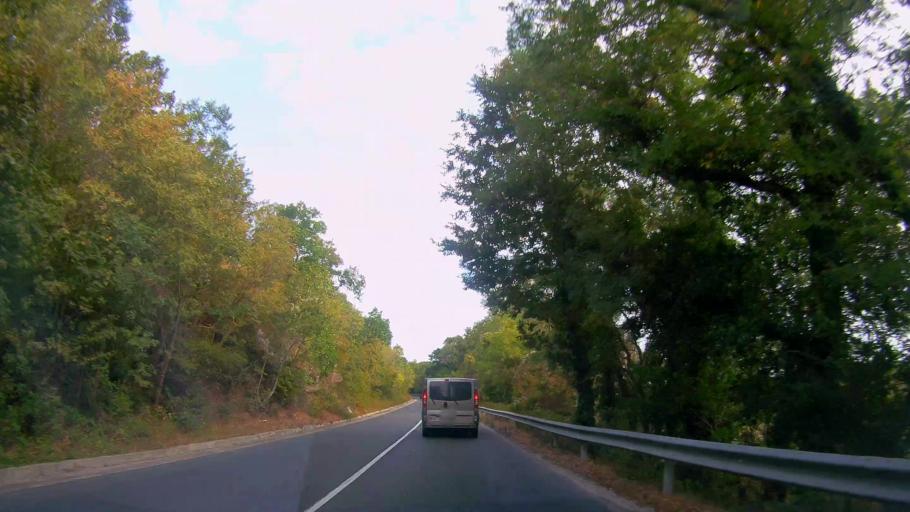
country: BG
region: Burgas
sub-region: Obshtina Primorsko
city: Primorsko
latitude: 42.3190
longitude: 27.7317
